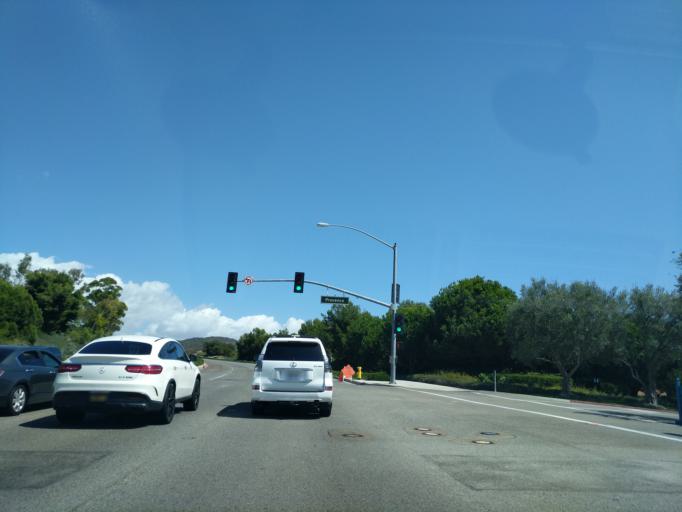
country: US
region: California
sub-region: Orange County
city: San Joaquin Hills
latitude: 33.5836
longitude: -117.8388
